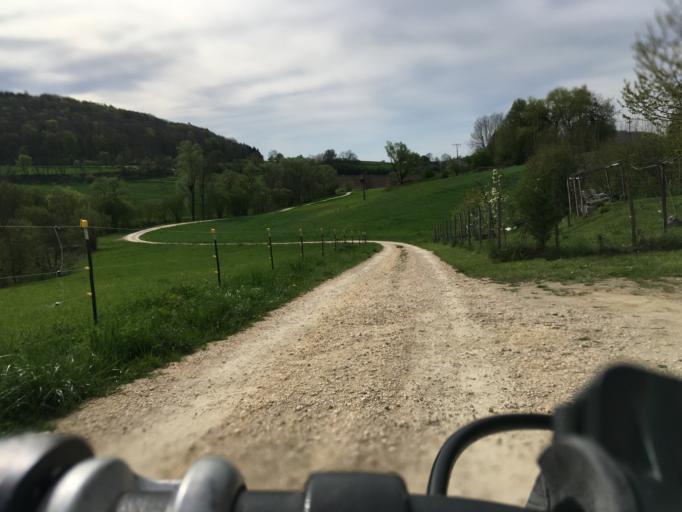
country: DE
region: Baden-Wuerttemberg
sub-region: Freiburg Region
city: Hilzingen
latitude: 47.7521
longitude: 8.7970
